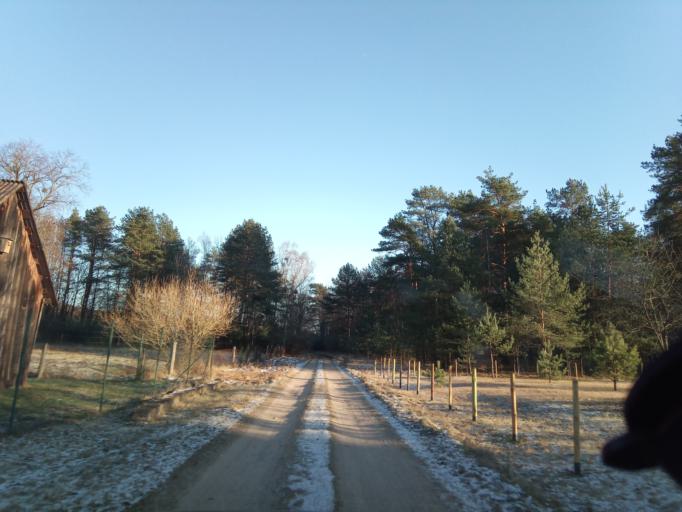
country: LT
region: Alytaus apskritis
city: Druskininkai
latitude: 53.9736
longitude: 23.9506
